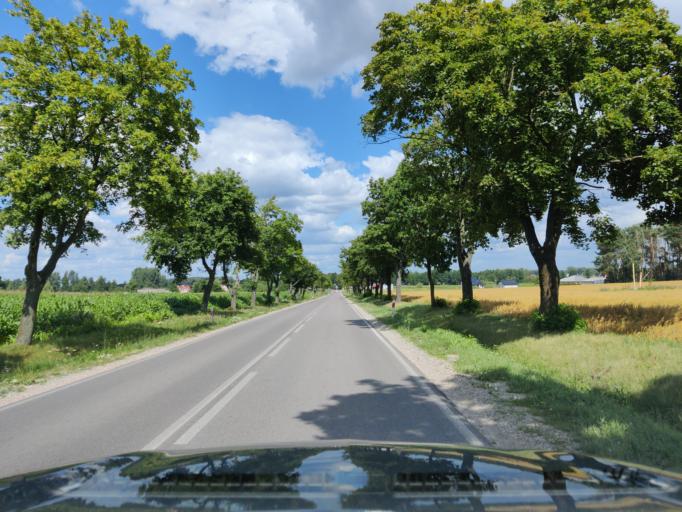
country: PL
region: Masovian Voivodeship
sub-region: Powiat wegrowski
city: Grebkow
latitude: 52.2625
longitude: 21.9045
